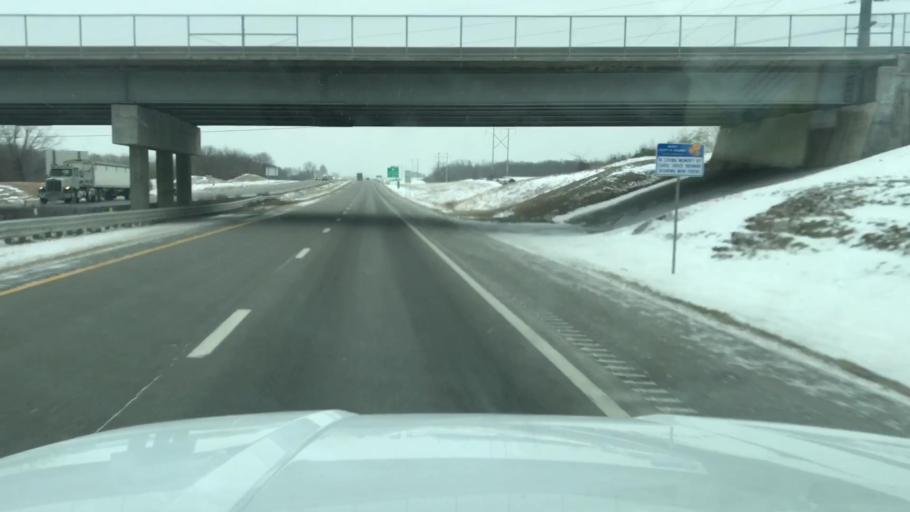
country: US
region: Missouri
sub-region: Buchanan County
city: Saint Joseph
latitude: 39.7700
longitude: -94.7928
